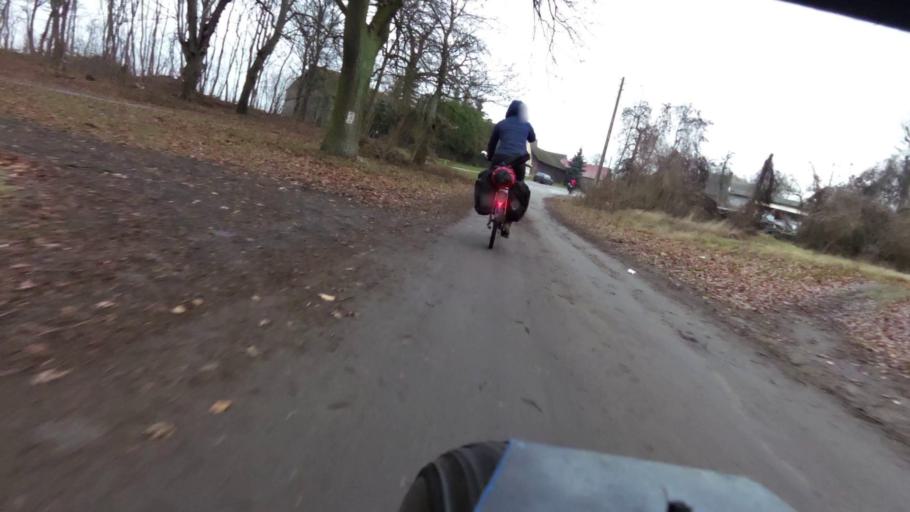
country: PL
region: Lubusz
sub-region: Powiat gorzowski
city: Witnica
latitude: 52.6775
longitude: 14.8039
